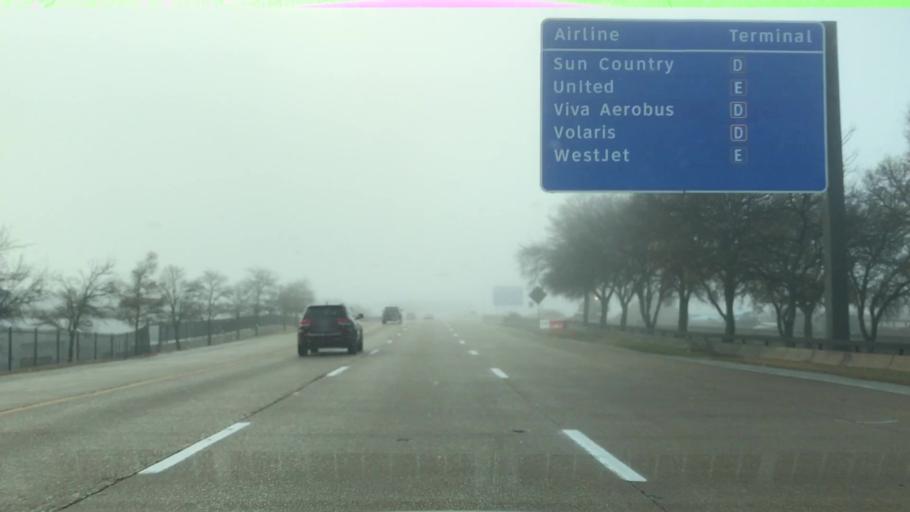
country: US
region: Texas
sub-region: Tarrant County
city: Grapevine
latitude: 32.9134
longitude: -97.0410
